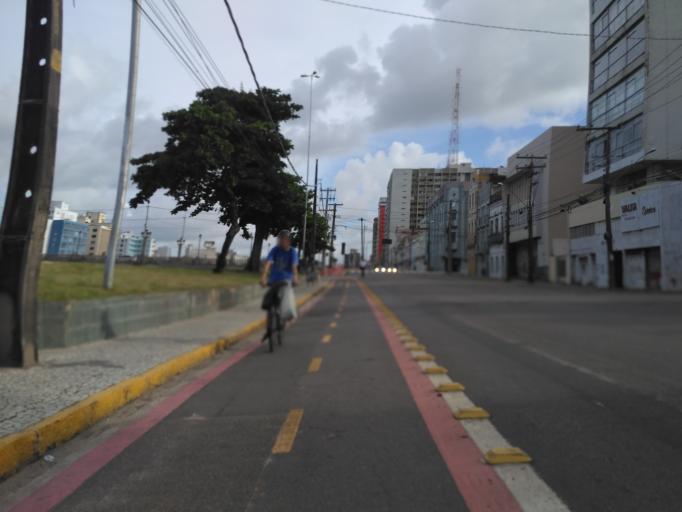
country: BR
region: Pernambuco
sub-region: Recife
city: Recife
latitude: -8.0586
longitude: -34.8794
